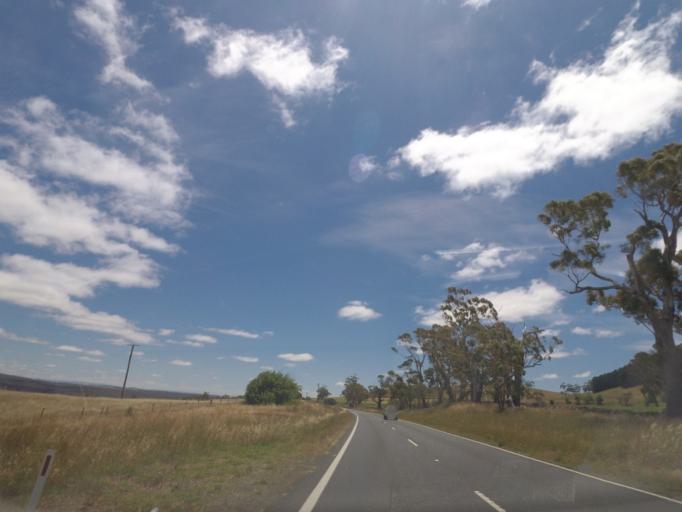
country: AU
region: Victoria
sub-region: Mount Alexander
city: Castlemaine
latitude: -37.2732
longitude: 144.1463
